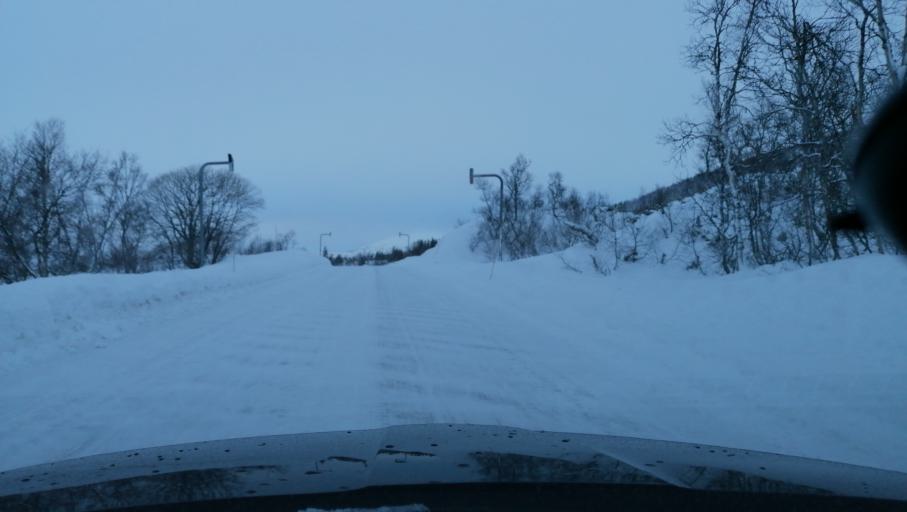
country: NO
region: Aust-Agder
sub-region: Bykle
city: Hovden
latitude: 59.6357
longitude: 7.4538
